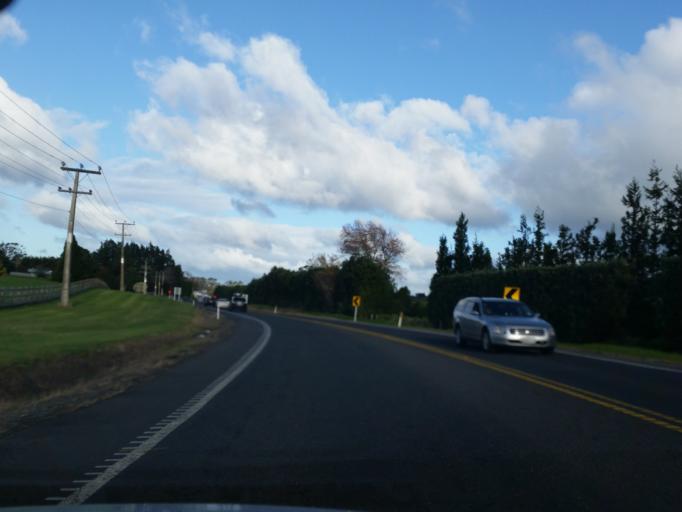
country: NZ
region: Bay of Plenty
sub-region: Western Bay of Plenty District
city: Katikati
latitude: -37.5953
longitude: 175.9118
